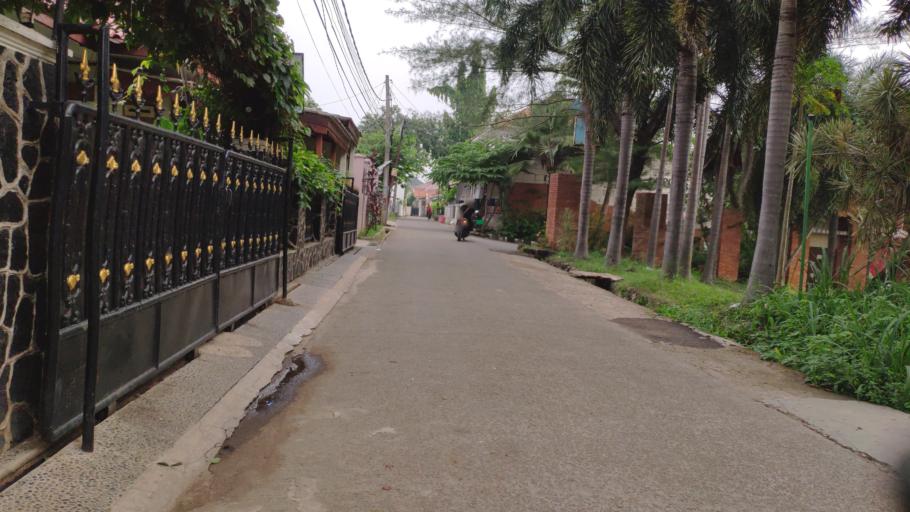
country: ID
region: West Java
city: Depok
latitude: -6.3766
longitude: 106.7987
